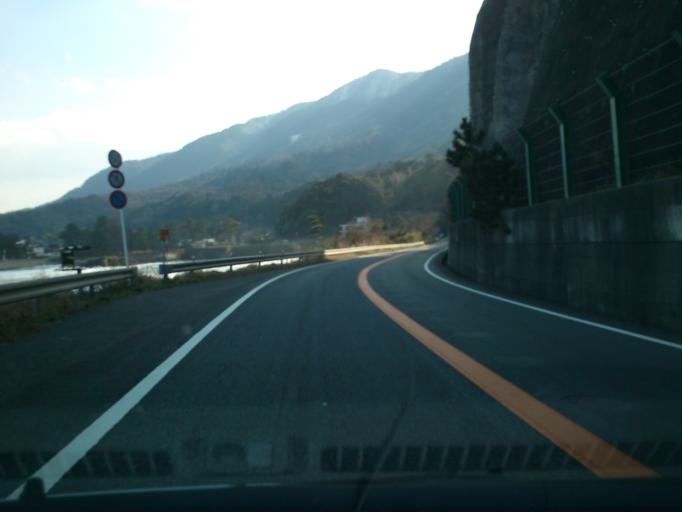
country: JP
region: Kyoto
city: Miyazu
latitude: 35.5275
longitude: 135.2726
